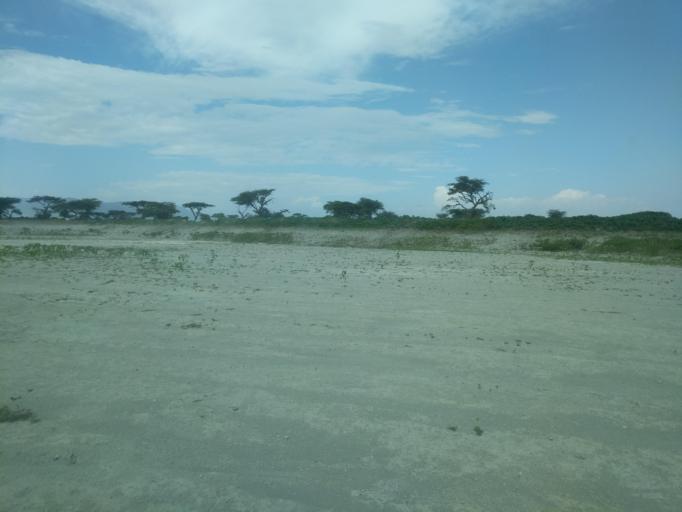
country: ET
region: Oromiya
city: Ziway
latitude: 7.6910
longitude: 38.6469
